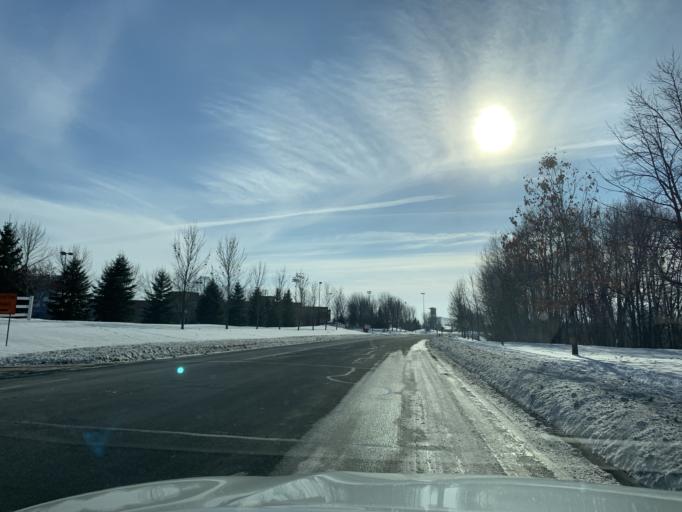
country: US
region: Minnesota
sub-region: Anoka County
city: Columbus
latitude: 45.2466
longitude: -93.0350
